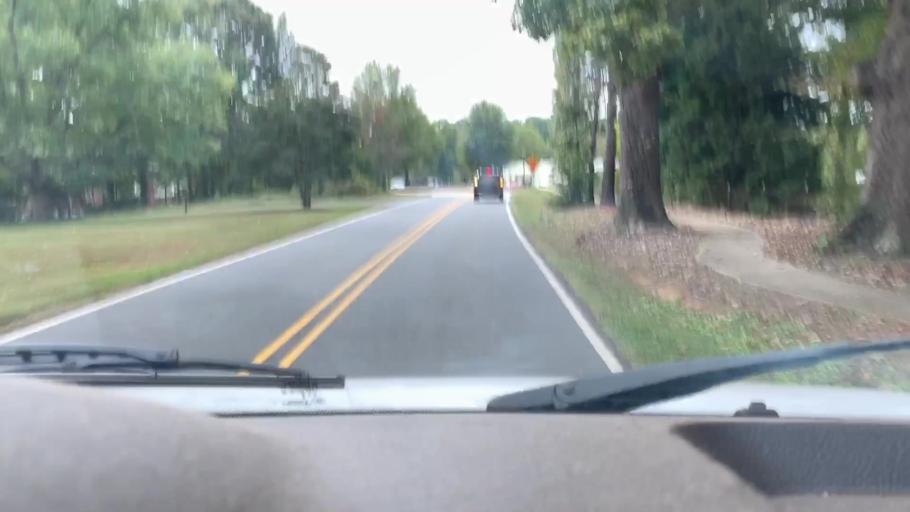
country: US
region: North Carolina
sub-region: Mecklenburg County
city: Cornelius
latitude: 35.4602
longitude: -80.8678
